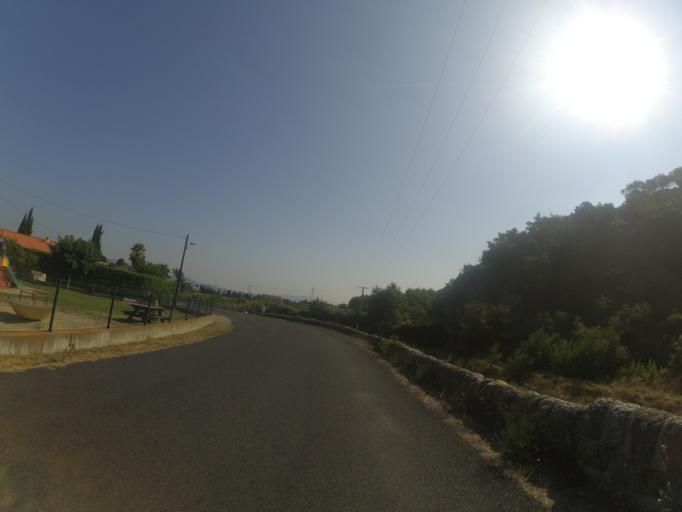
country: FR
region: Languedoc-Roussillon
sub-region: Departement des Pyrenees-Orientales
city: Ille-sur-Tet
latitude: 42.6518
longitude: 2.6233
